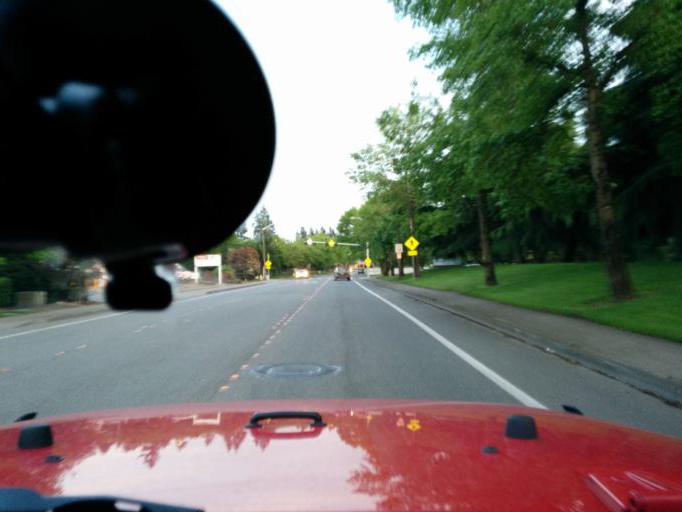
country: US
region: Washington
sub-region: King County
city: Redmond
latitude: 47.6744
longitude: -122.1027
